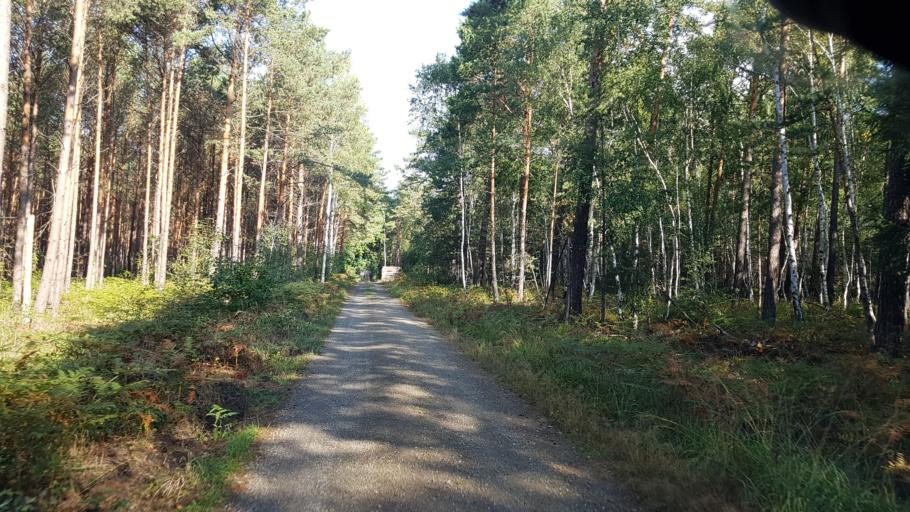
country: DE
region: Brandenburg
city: Plessa
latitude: 51.5232
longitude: 13.6389
